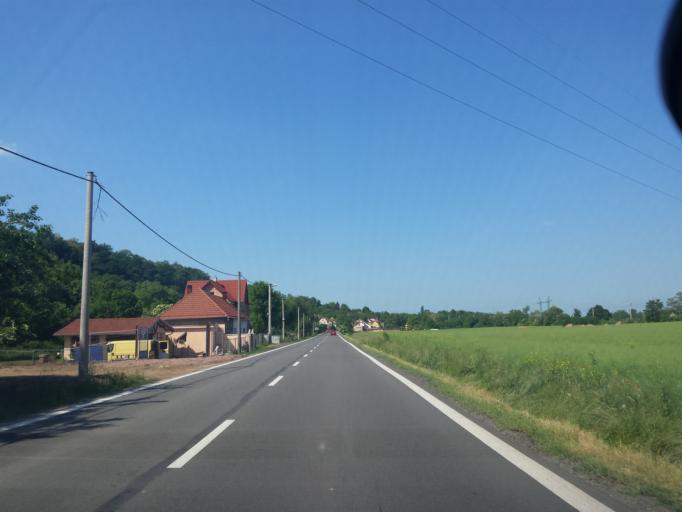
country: CZ
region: Central Bohemia
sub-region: Okres Melnik
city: Veltrusy
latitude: 50.2957
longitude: 14.3119
